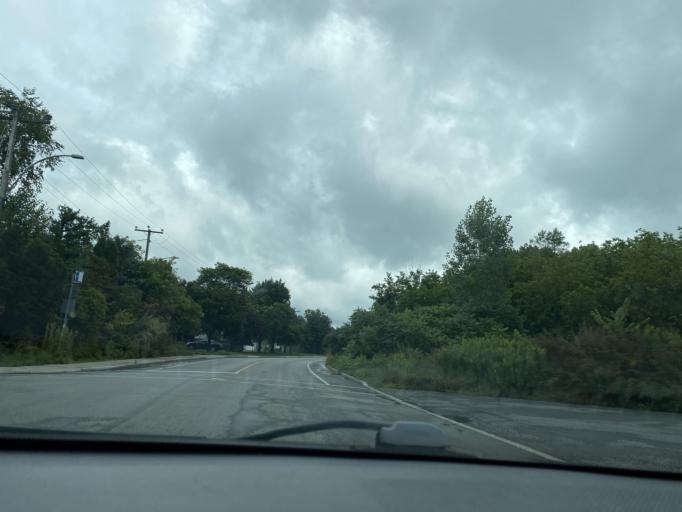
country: CA
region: Quebec
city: Baie-D'Urfe
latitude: 45.4376
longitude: -73.9012
